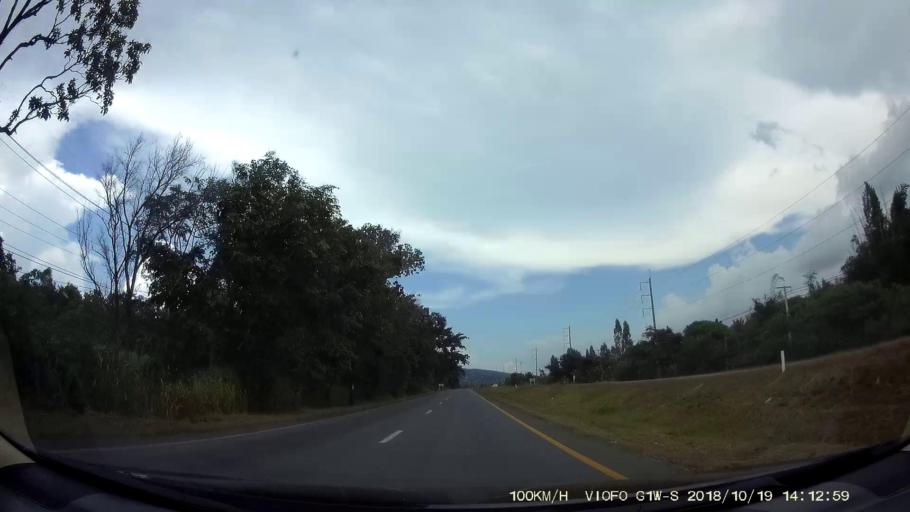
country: TH
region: Chaiyaphum
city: Khon Sawan
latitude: 15.9551
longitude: 102.1780
